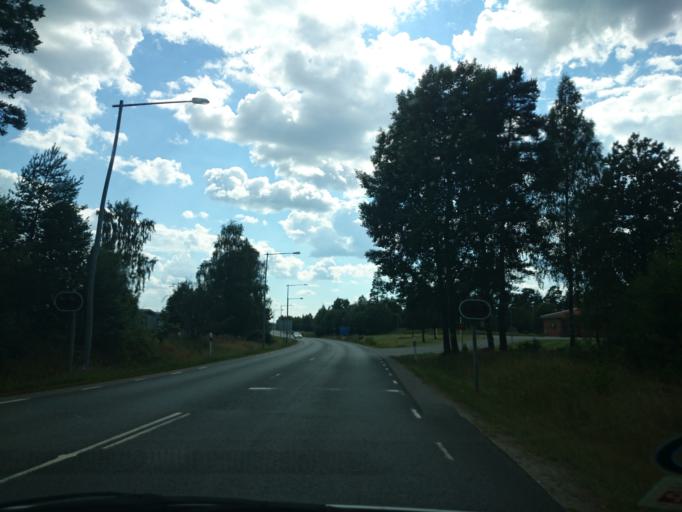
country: SE
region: Joenkoeping
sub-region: Varnamo Kommun
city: Varnamo
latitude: 57.1809
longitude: 14.0062
